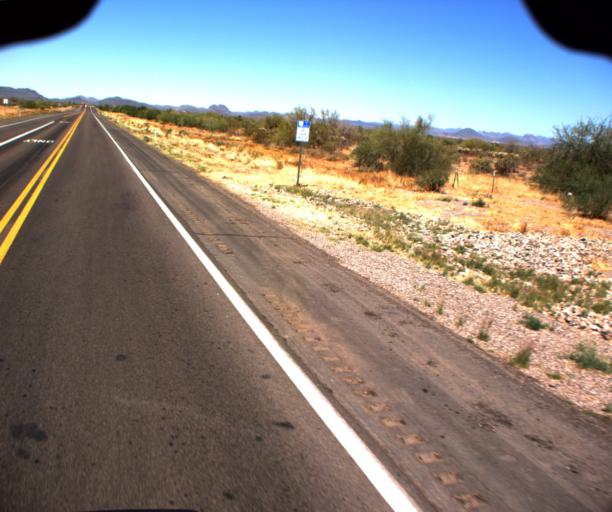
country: US
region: Arizona
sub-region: Maricopa County
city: Anthem
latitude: 33.7978
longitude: -112.2062
